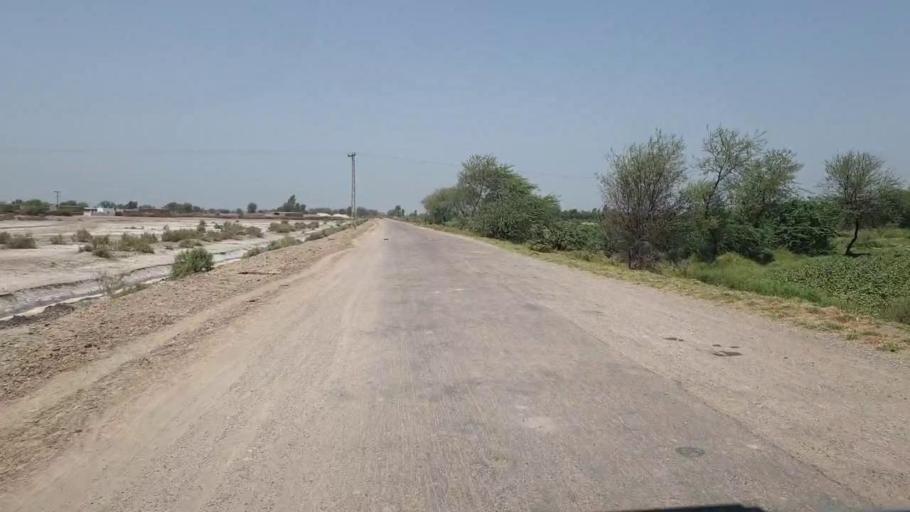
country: PK
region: Sindh
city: Nawabshah
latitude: 26.3584
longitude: 68.4024
